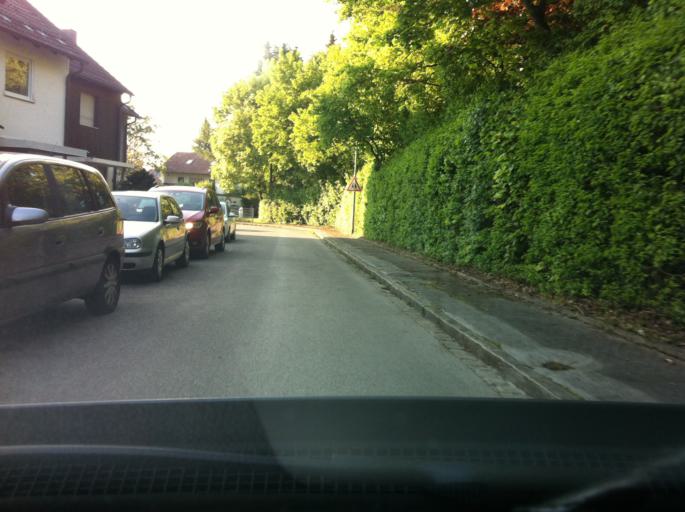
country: DE
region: Bavaria
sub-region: Upper Bavaria
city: Oberhaching
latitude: 48.0443
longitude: 11.5967
